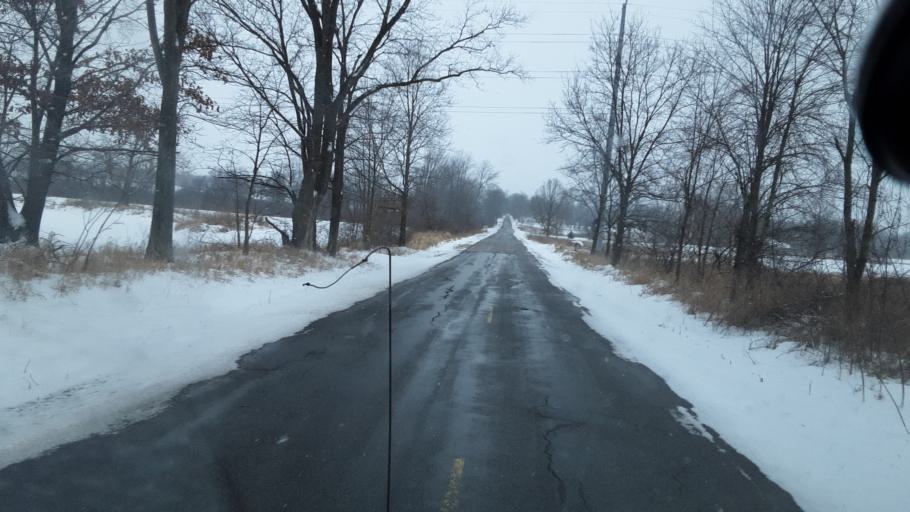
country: US
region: Michigan
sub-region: Ingham County
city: Leslie
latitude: 42.4367
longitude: -84.4714
